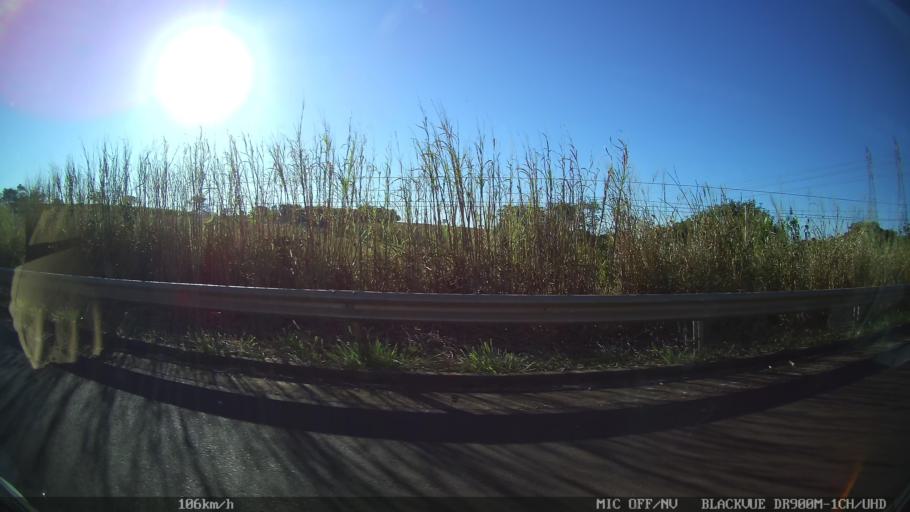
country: BR
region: Sao Paulo
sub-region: Olimpia
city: Olimpia
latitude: -20.7079
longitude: -48.9647
